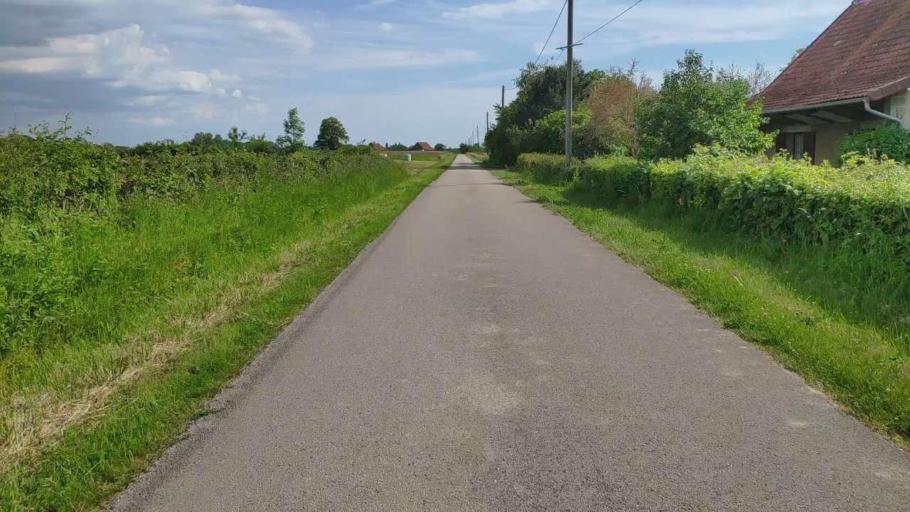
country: FR
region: Franche-Comte
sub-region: Departement du Jura
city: Bletterans
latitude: 46.8171
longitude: 5.3796
